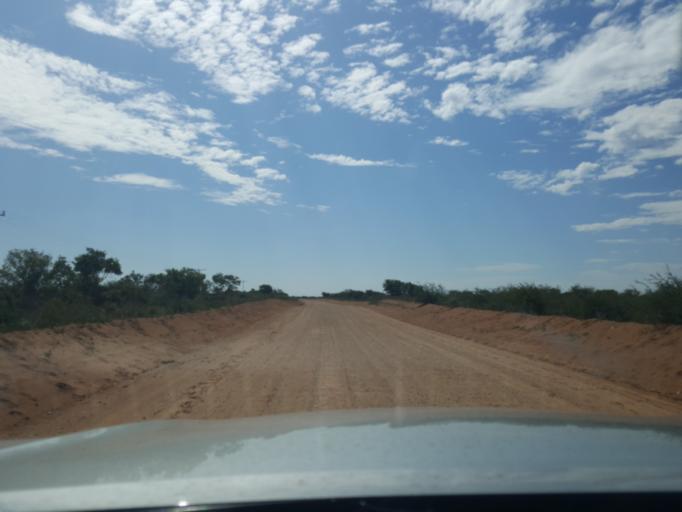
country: BW
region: Kweneng
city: Khudumelapye
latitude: -23.8456
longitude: 24.8615
